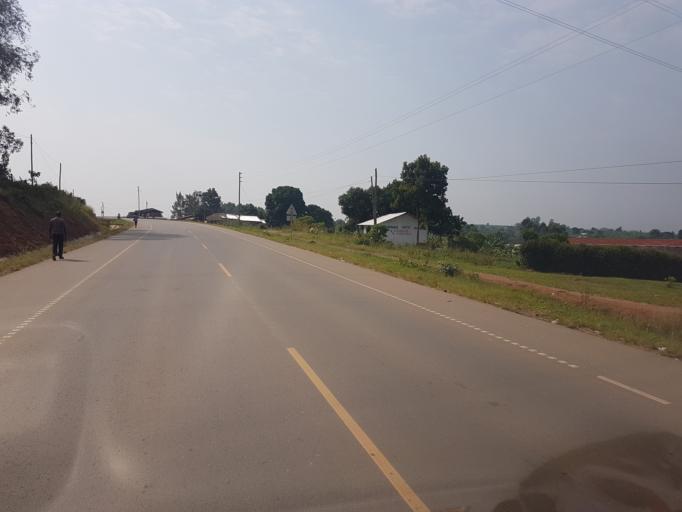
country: UG
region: Western Region
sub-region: Mbarara District
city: Bwizibwera
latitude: -0.6366
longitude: 30.6088
